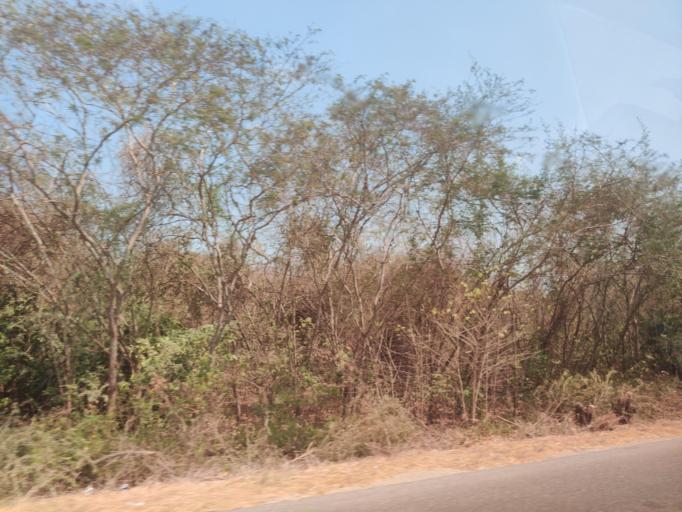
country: CO
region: Bolivar
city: Turbana
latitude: 10.2761
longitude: -75.5309
